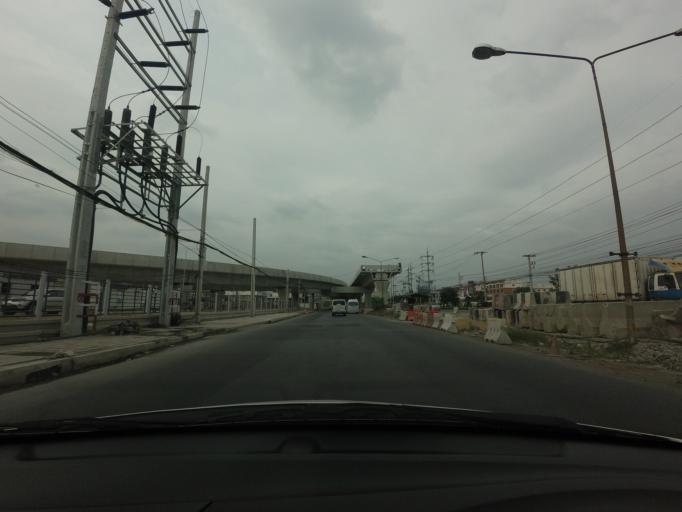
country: TH
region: Samut Prakan
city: Samut Prakan
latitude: 13.5574
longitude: 100.6126
